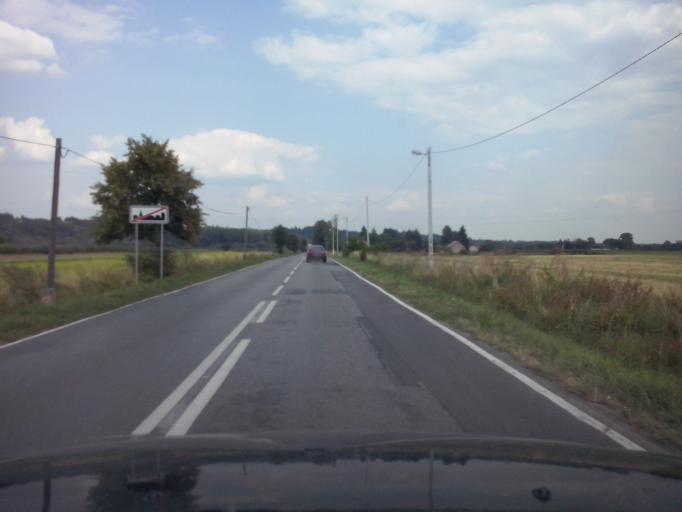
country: PL
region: Subcarpathian Voivodeship
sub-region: Powiat nizanski
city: Krzeszow
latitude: 50.4004
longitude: 22.3176
